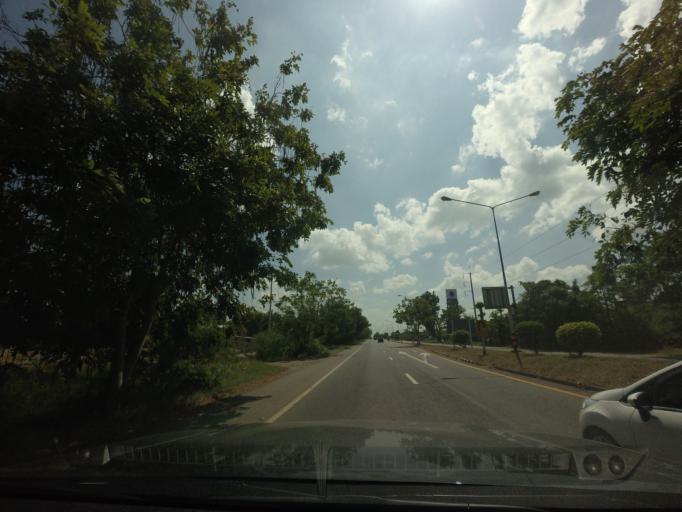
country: TH
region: Phetchabun
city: Nong Phai
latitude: 16.0228
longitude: 101.0740
